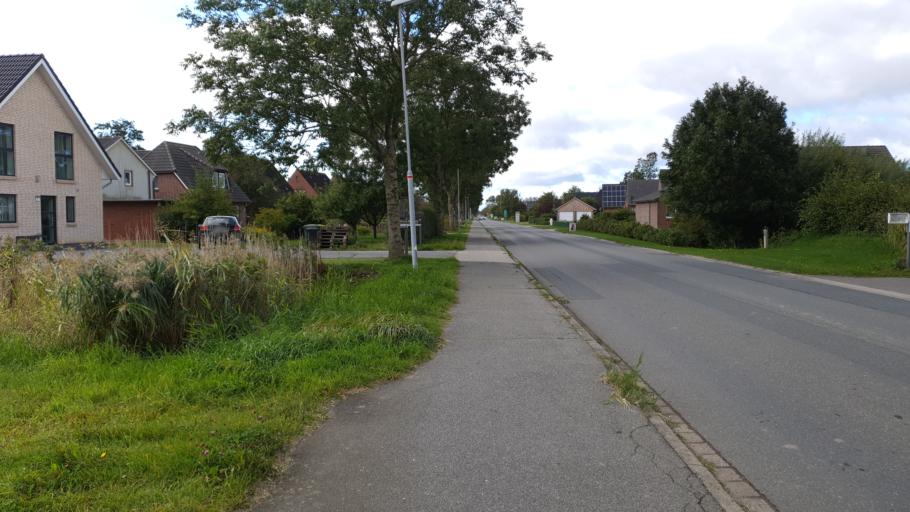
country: DE
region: Schleswig-Holstein
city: Elisabeth-Sophien-Koog
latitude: 54.4886
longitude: 8.8829
